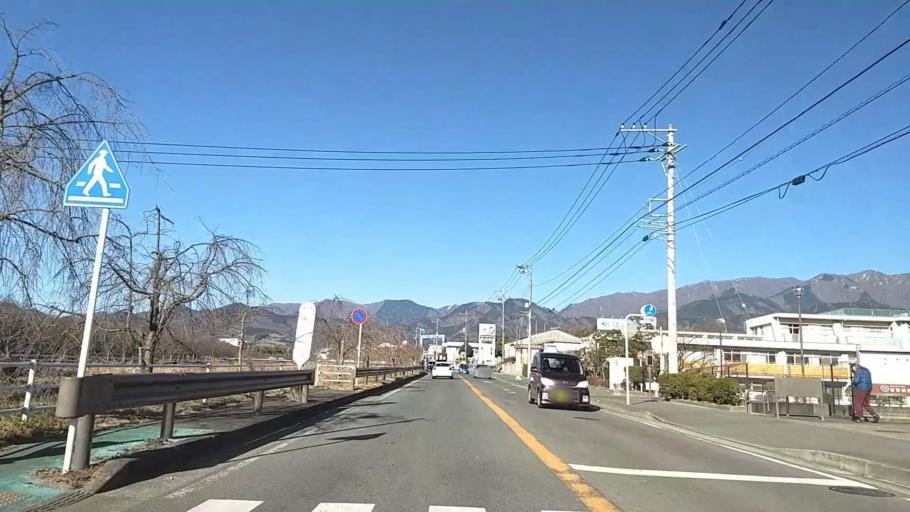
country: JP
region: Kanagawa
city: Hadano
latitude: 35.3854
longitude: 139.1939
